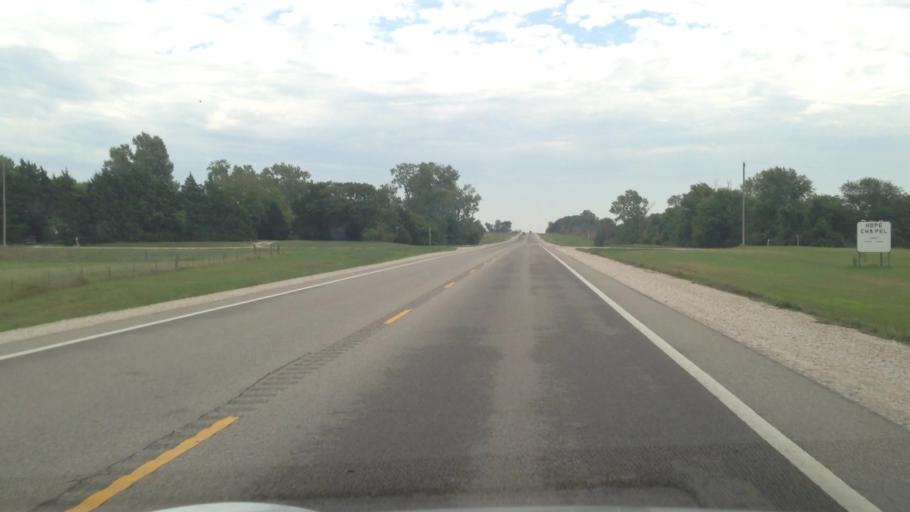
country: US
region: Kansas
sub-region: Allen County
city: Iola
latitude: 37.9098
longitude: -95.1175
